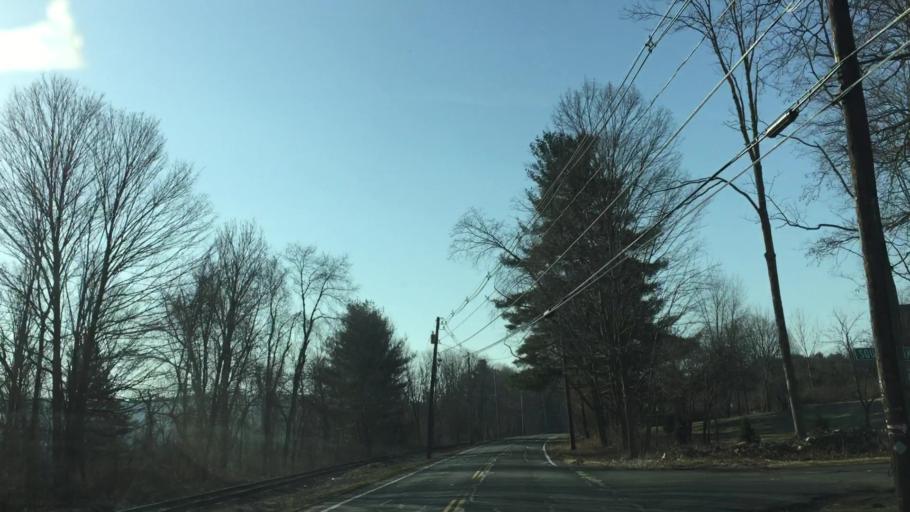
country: US
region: Massachusetts
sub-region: Berkshire County
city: Great Barrington
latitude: 42.2230
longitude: -73.3586
